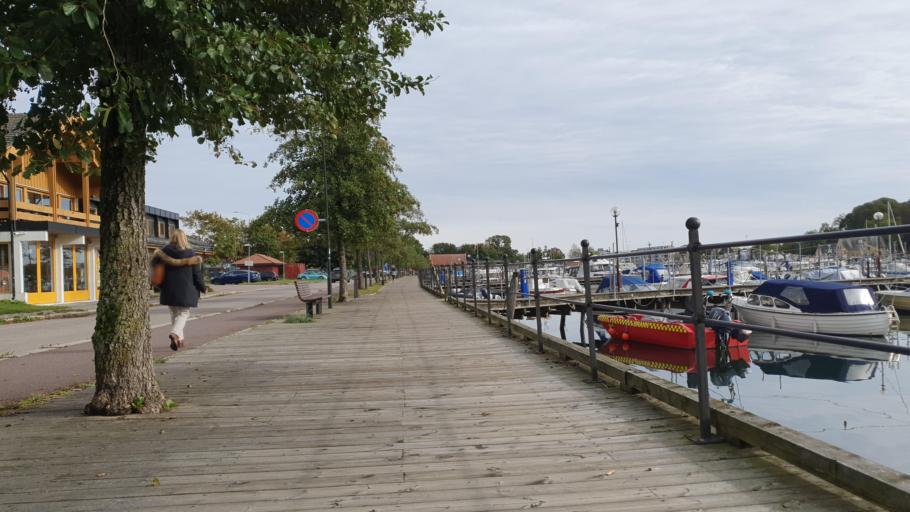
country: NO
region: Vestfold
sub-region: Tonsberg
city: Tonsberg
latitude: 59.2638
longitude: 10.4095
